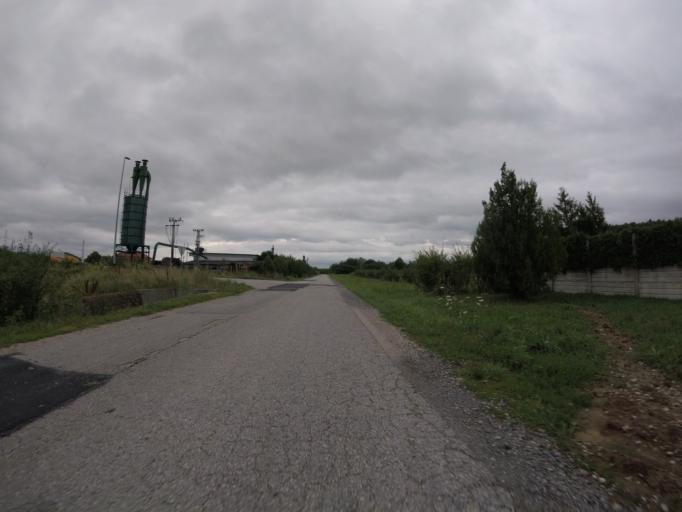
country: HR
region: Zagrebacka
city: Turopolje
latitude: 45.6555
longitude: 16.1244
